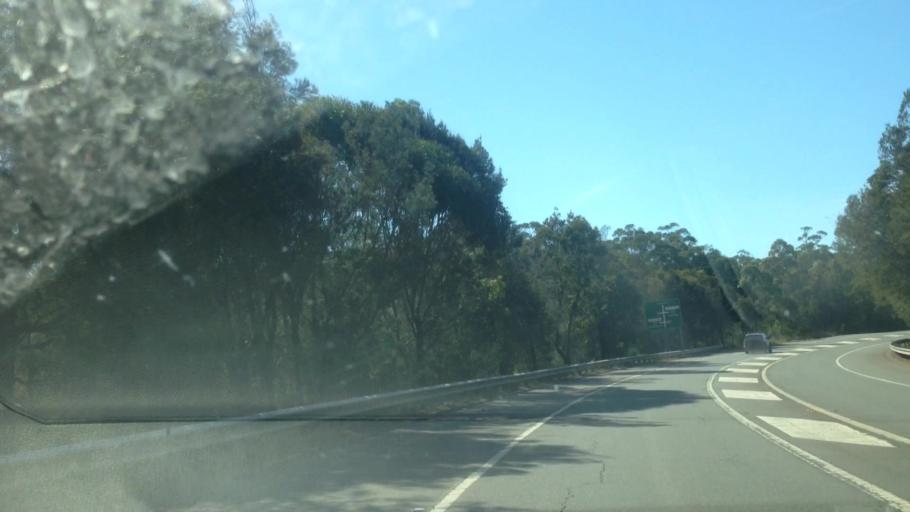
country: AU
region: New South Wales
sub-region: Lake Macquarie Shire
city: Toronto
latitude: -32.9860
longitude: 151.5157
